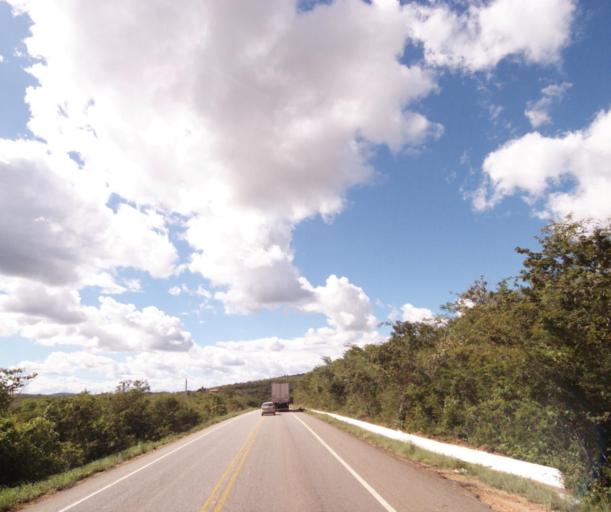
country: BR
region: Bahia
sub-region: Caetite
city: Caetite
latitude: -14.1413
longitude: -42.3793
